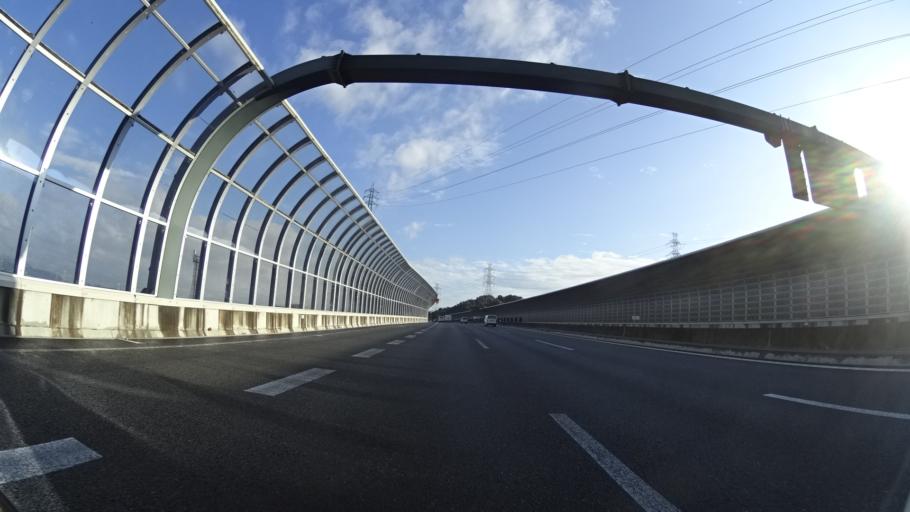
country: JP
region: Osaka
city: Hirakata
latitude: 34.7957
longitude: 135.7010
